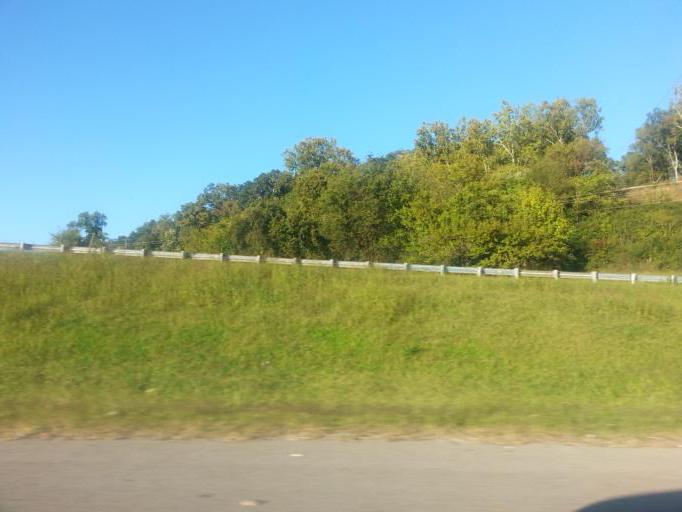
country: US
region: Tennessee
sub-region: Knox County
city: Knoxville
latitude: 35.9989
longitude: -83.9555
